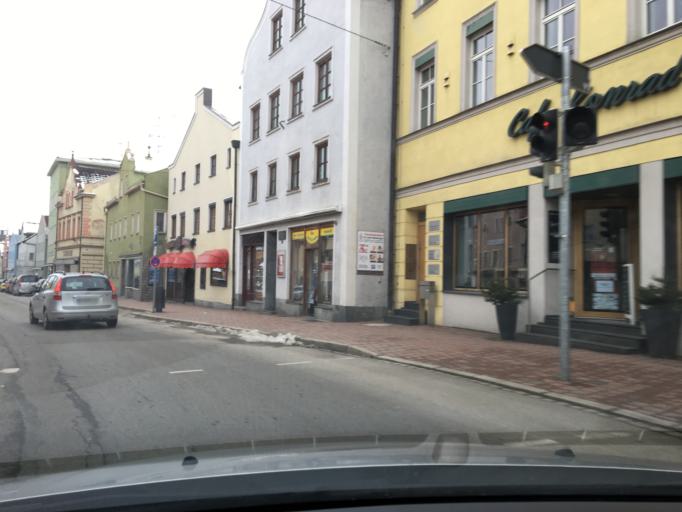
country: DE
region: Bavaria
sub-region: Lower Bavaria
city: Vilsbiburg
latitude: 48.4499
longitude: 12.3531
